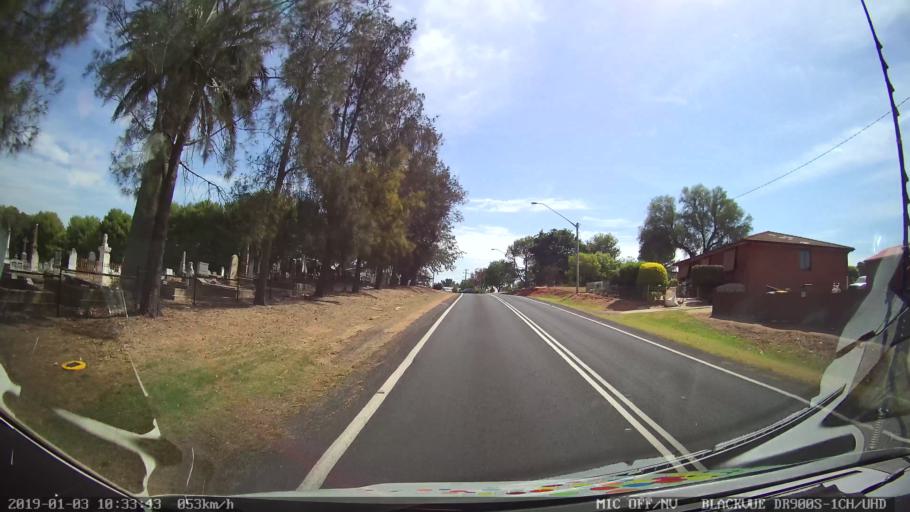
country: AU
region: New South Wales
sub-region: Young
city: Young
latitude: -34.3263
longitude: 148.2894
